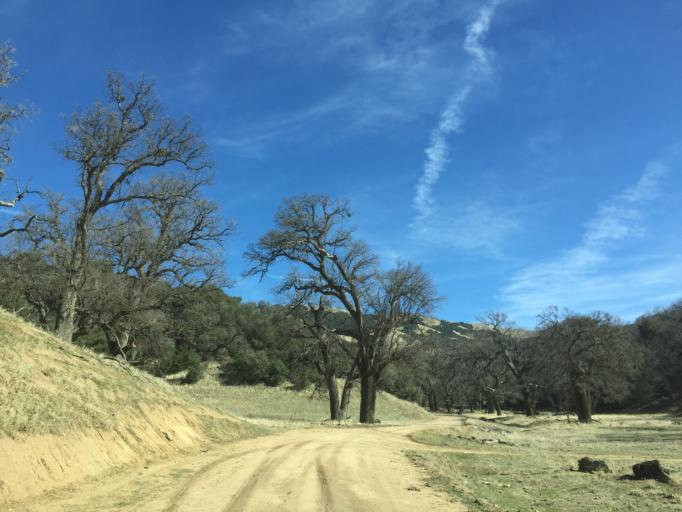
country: US
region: California
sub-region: Kern County
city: Stallion Springs
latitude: 34.9147
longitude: -118.6870
